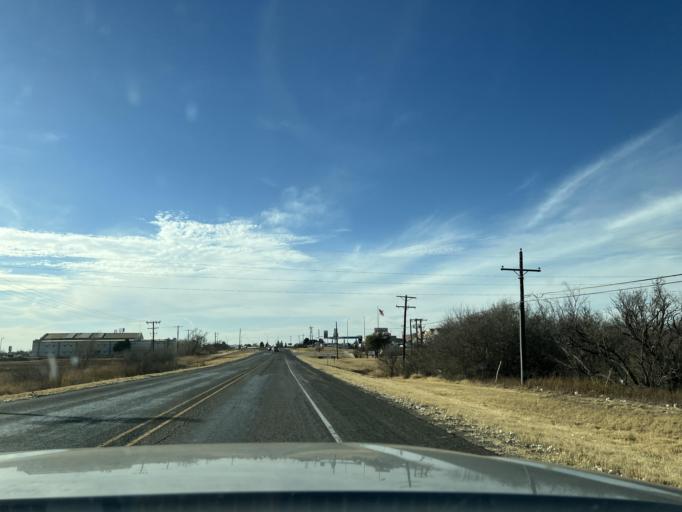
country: US
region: Texas
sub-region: Scurry County
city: Snyder
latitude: 32.7043
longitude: -100.8623
